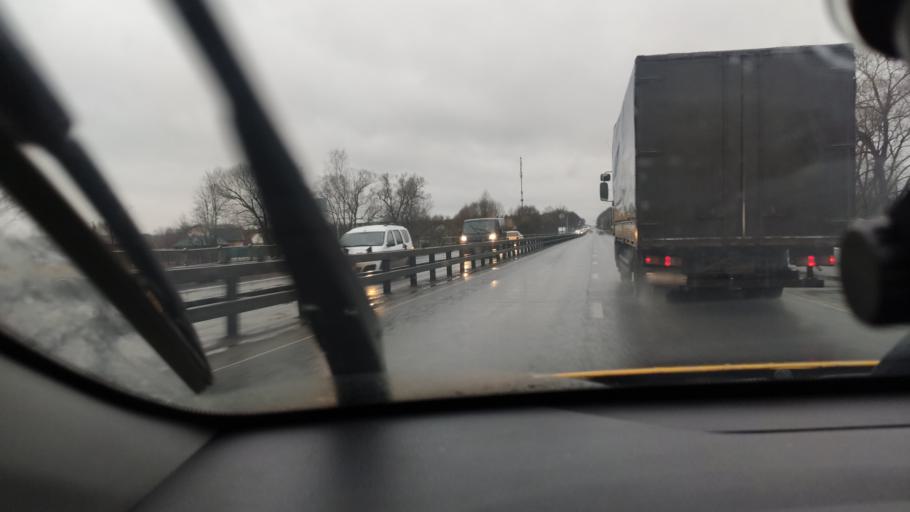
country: RU
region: Moskovskaya
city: Troitsk
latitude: 55.3530
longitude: 37.3410
